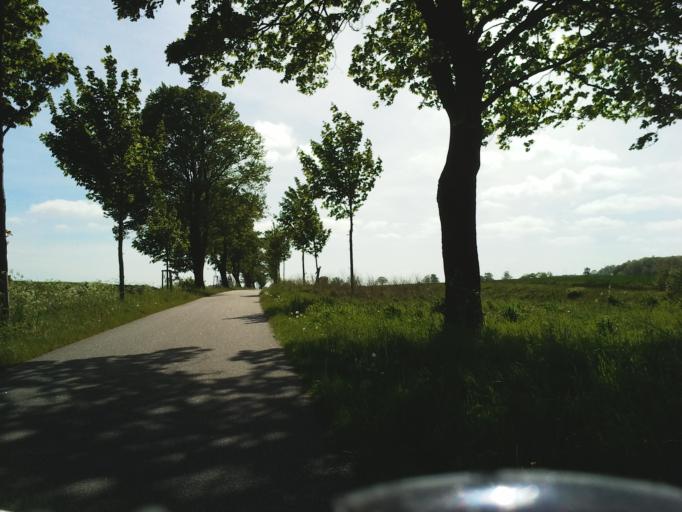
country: DE
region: Mecklenburg-Vorpommern
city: Papendorf
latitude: 54.0406
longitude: 12.1091
